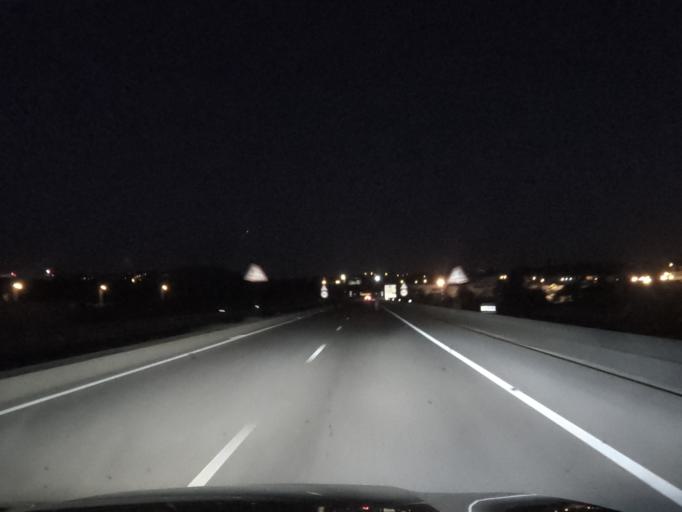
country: PT
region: Faro
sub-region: Loule
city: Loule
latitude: 37.1342
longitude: -8.0404
